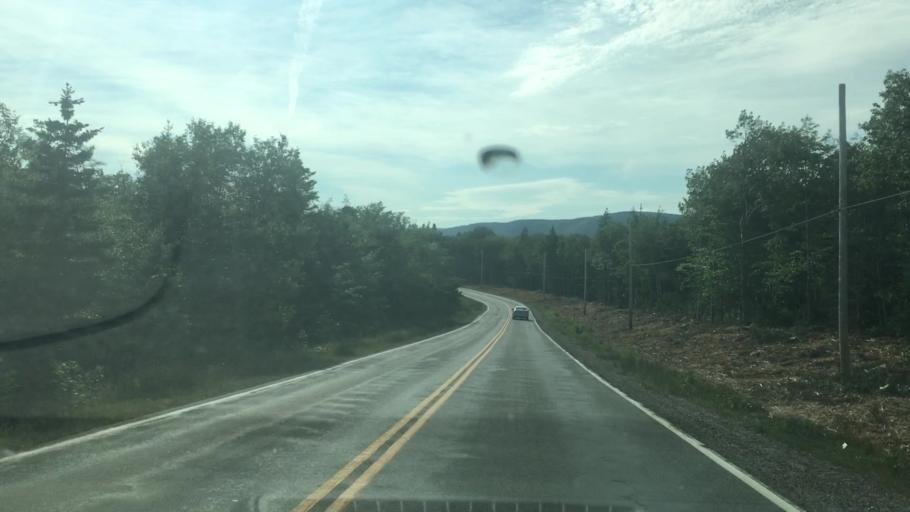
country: CA
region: Nova Scotia
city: Sydney Mines
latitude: 46.8819
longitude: -60.5116
